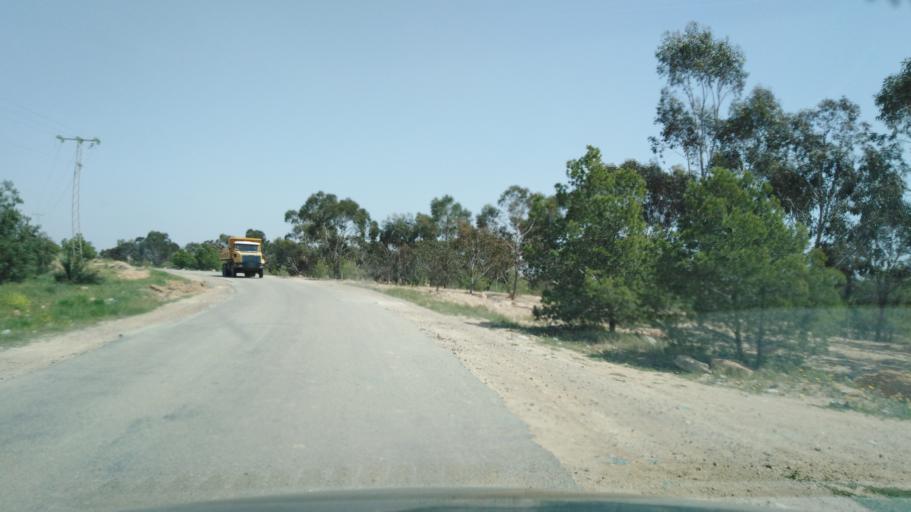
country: TN
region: Safaqis
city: Sfax
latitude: 34.7141
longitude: 10.5299
